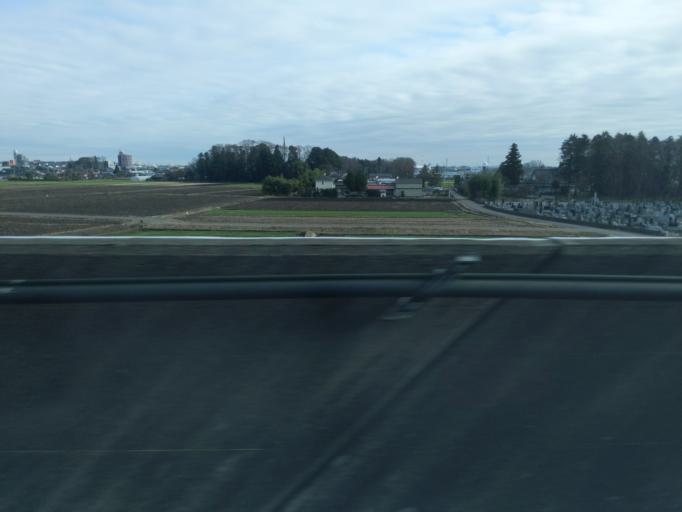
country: JP
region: Tochigi
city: Utsunomiya-shi
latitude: 36.5902
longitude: 139.9045
